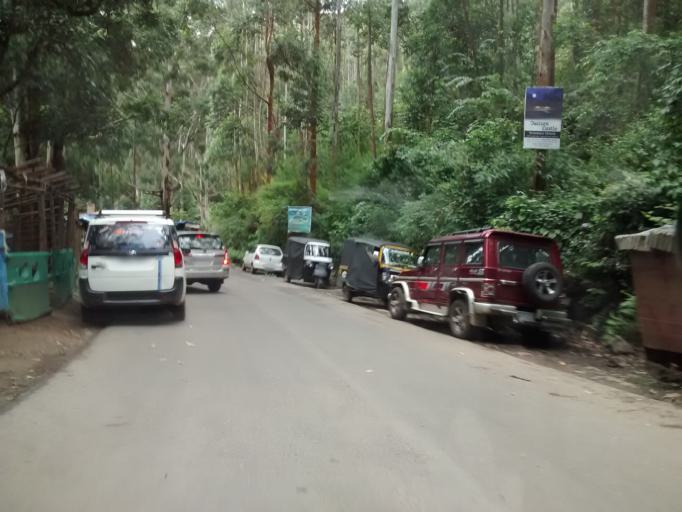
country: IN
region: Kerala
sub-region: Idukki
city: Munnar
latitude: 10.1207
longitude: 77.1528
